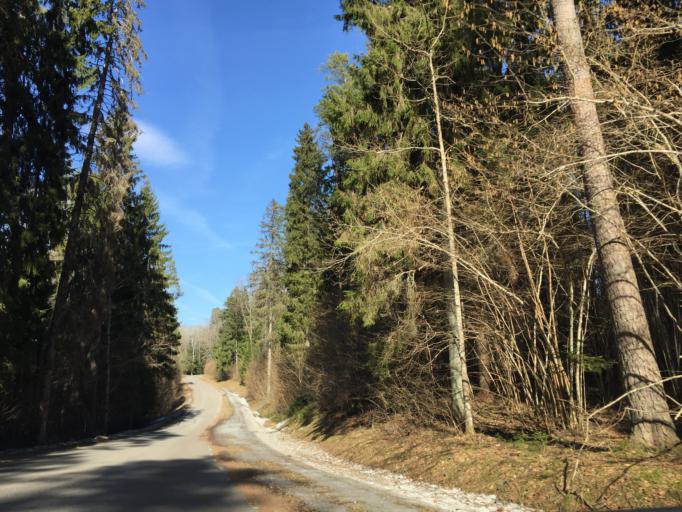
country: EE
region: Vorumaa
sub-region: Antsla vald
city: Vana-Antsla
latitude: 58.0304
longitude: 26.4756
